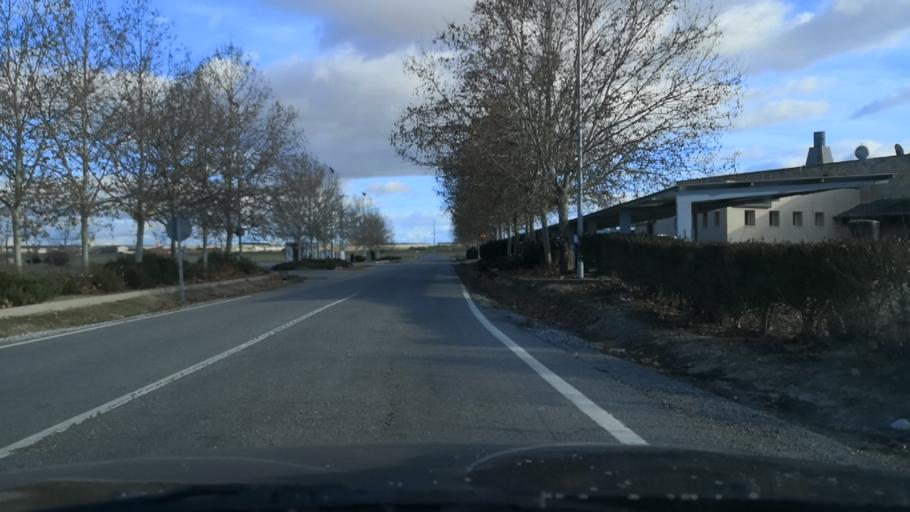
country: ES
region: Castille and Leon
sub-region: Provincia de Avila
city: Orbita
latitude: 41.0105
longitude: -4.6662
